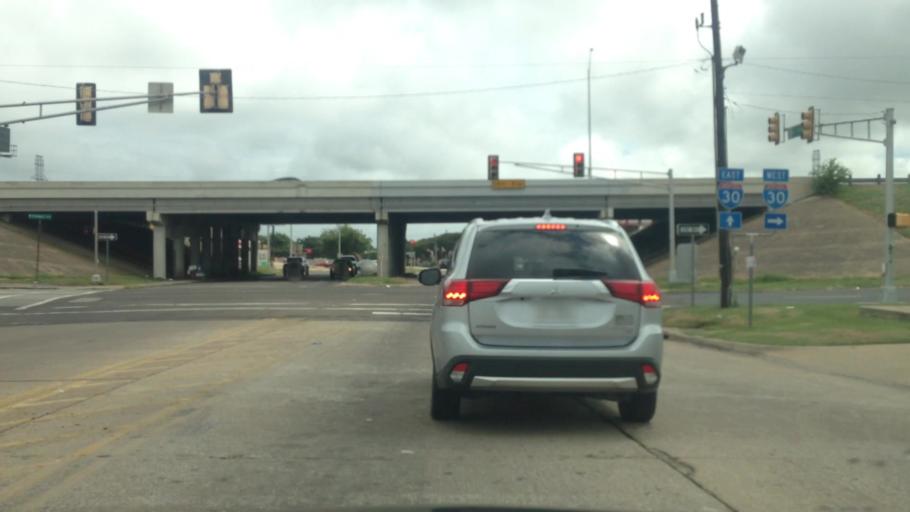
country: US
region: Texas
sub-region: Tarrant County
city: White Settlement
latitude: 32.7389
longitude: -97.4670
